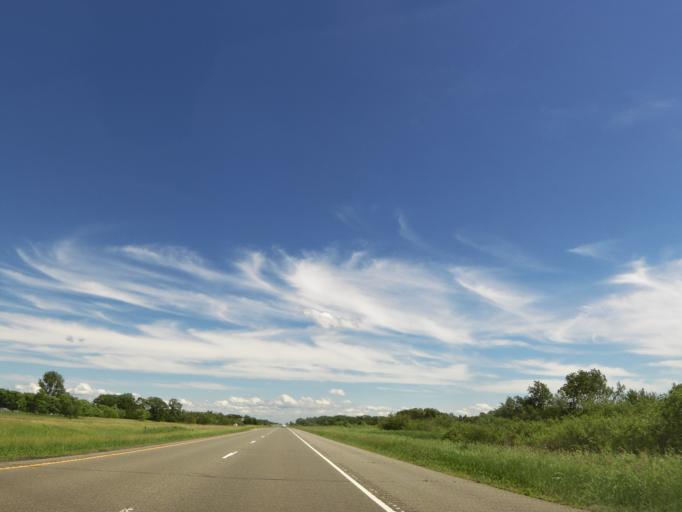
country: US
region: Minnesota
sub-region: Todd County
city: Staples
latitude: 46.3649
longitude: -94.8723
